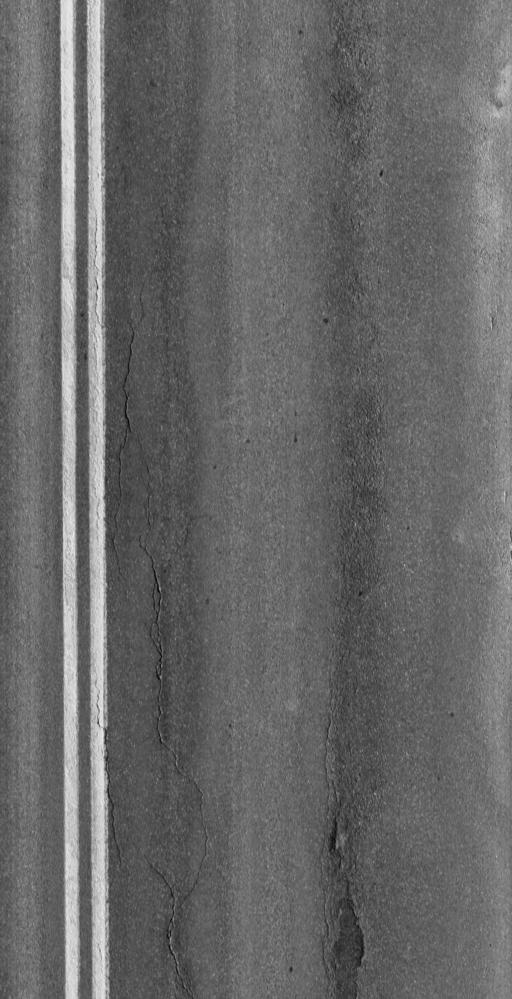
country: US
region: Vermont
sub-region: Chittenden County
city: Burlington
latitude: 44.3668
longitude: -73.2238
